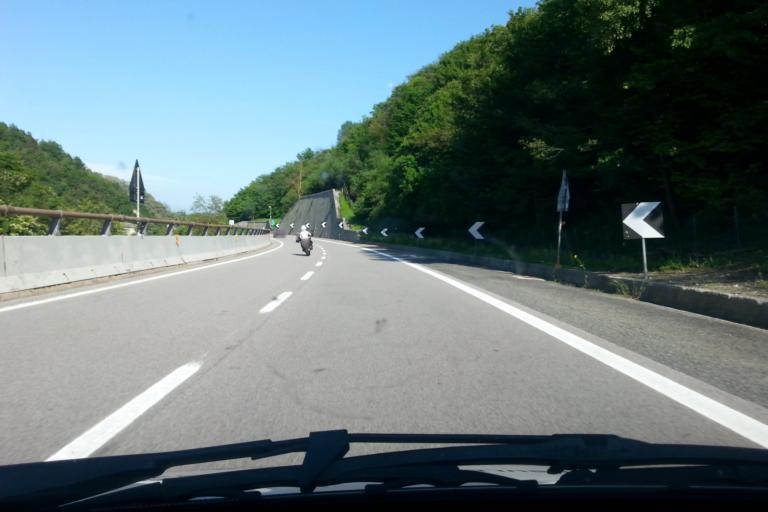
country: IT
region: Liguria
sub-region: Provincia di Savona
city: Valzemola
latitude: 44.3594
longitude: 8.1580
